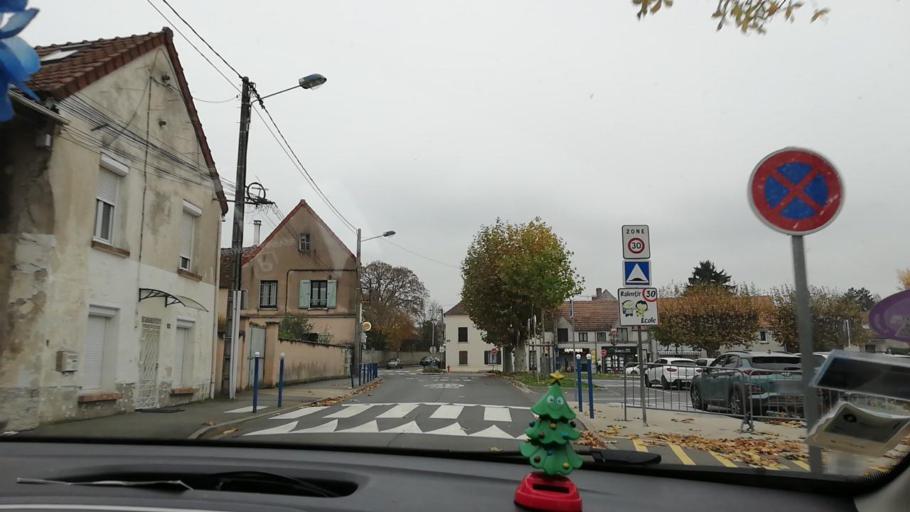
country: FR
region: Ile-de-France
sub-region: Departement de Seine-et-Marne
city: Saint-Mard
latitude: 49.0368
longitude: 2.6971
